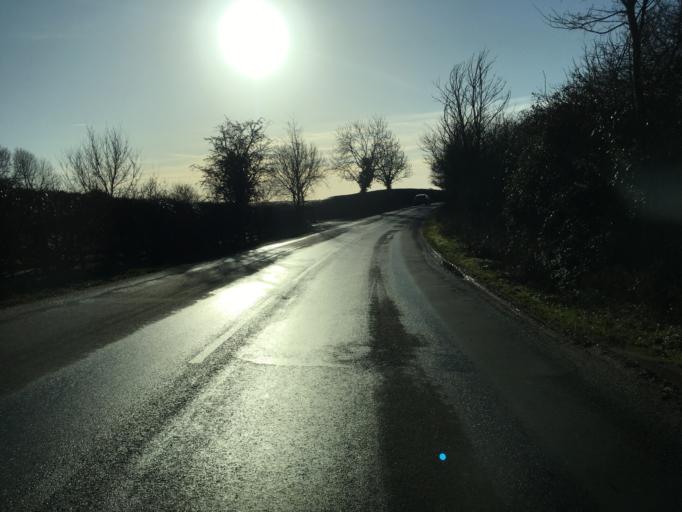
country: GB
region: England
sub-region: Warwickshire
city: Wellesbourne Mountford
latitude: 52.2035
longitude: -1.6164
